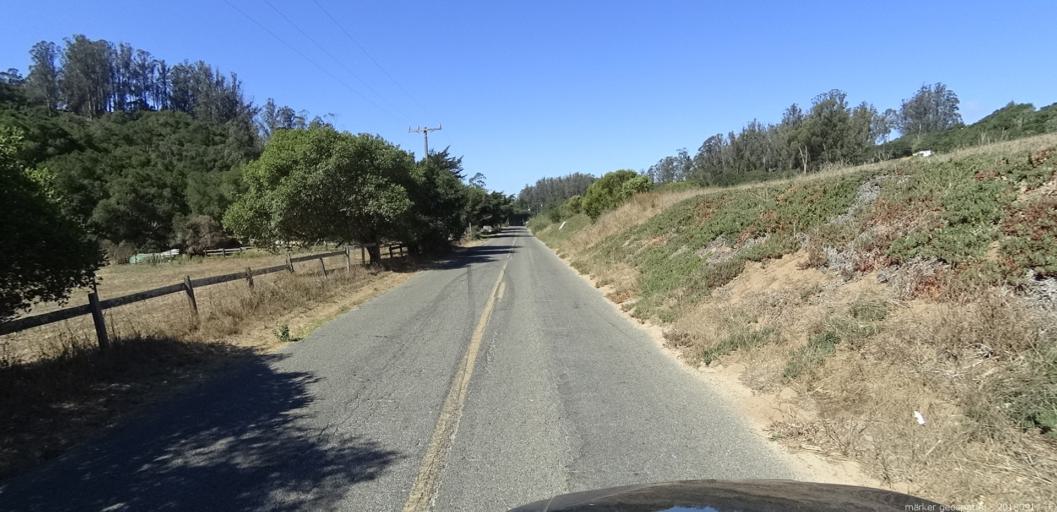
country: US
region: California
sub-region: Monterey County
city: Elkhorn
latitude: 36.8259
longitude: -121.7131
